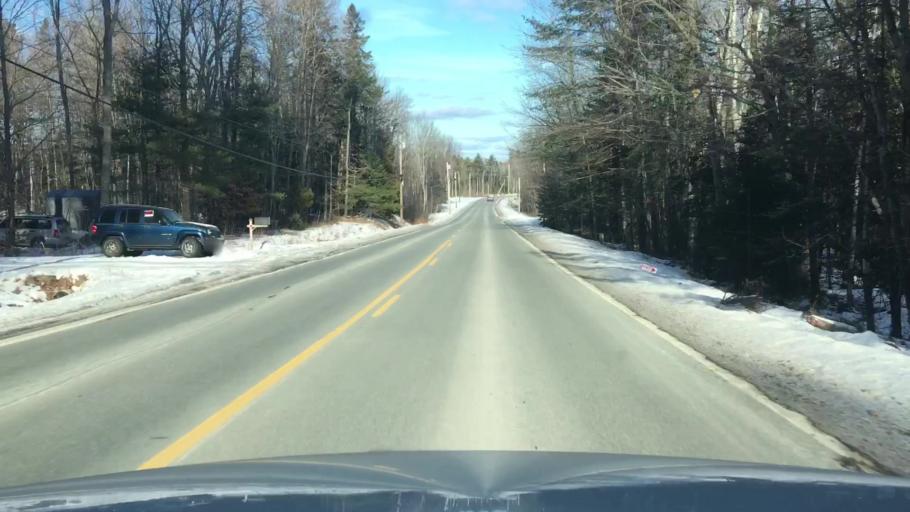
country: US
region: Maine
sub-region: Penobscot County
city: Holden
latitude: 44.7473
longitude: -68.6138
